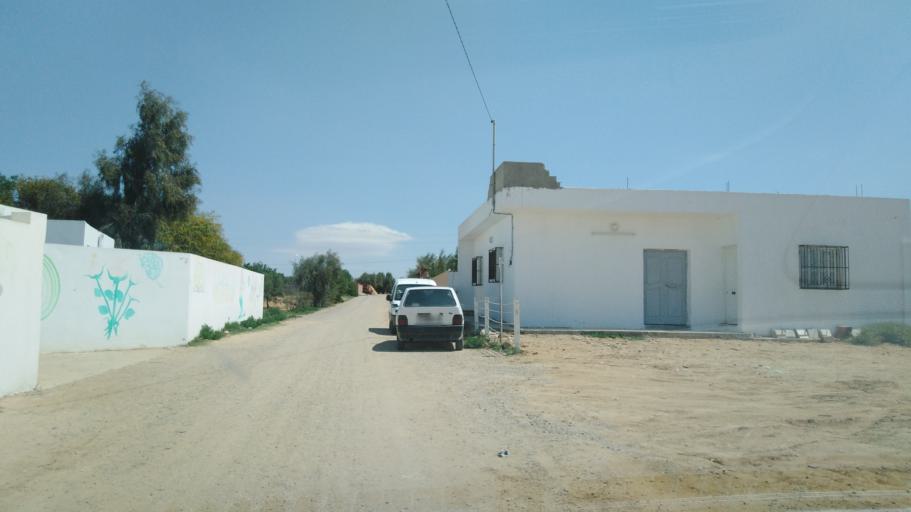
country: TN
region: Safaqis
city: Sfax
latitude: 34.7715
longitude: 10.5069
